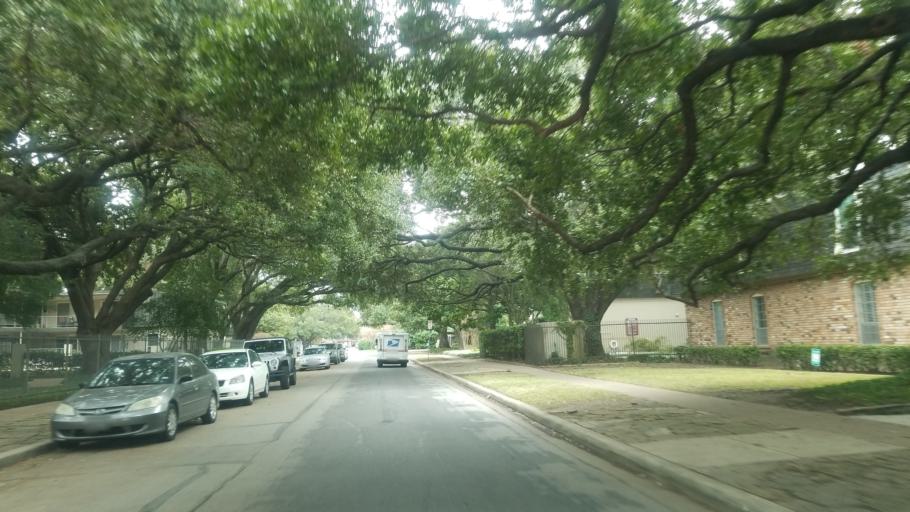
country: US
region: Texas
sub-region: Dallas County
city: Highland Park
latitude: 32.8189
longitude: -96.8315
